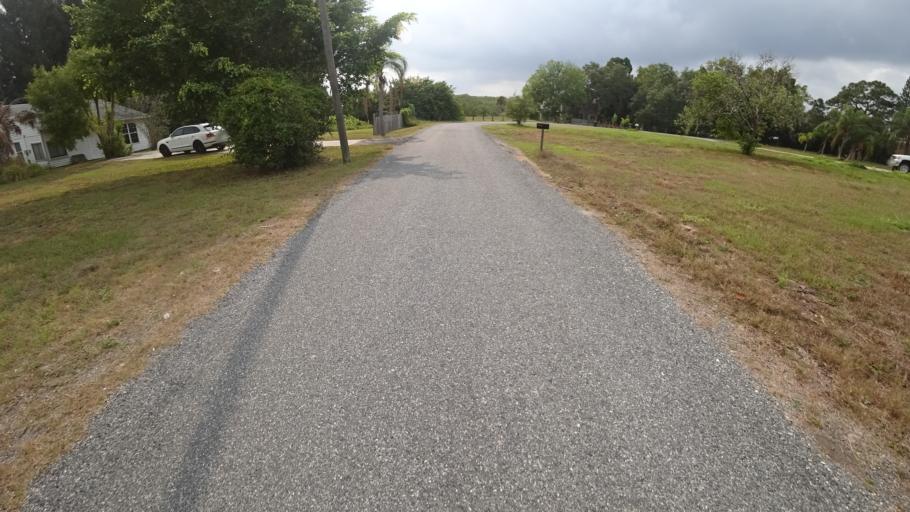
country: US
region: Florida
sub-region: Manatee County
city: Samoset
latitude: 27.4774
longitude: -82.4990
